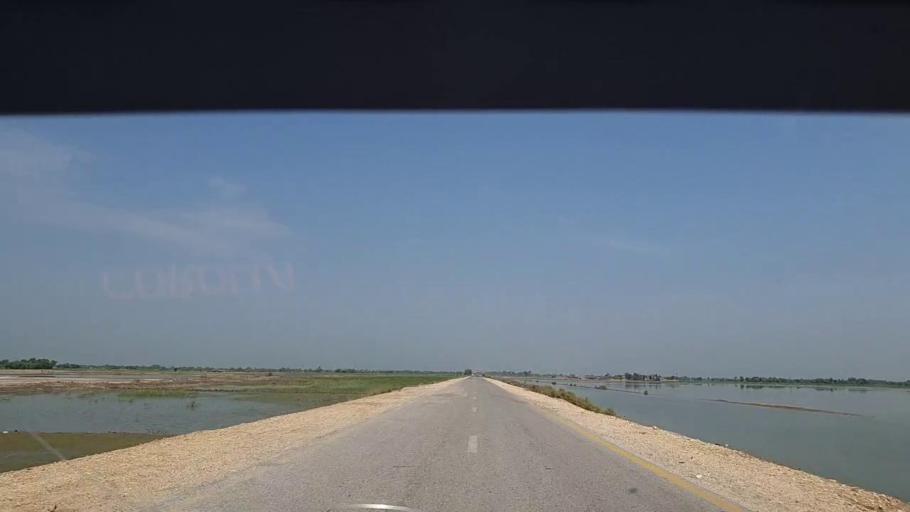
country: PK
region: Sindh
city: Rustam jo Goth
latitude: 28.0893
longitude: 68.7989
